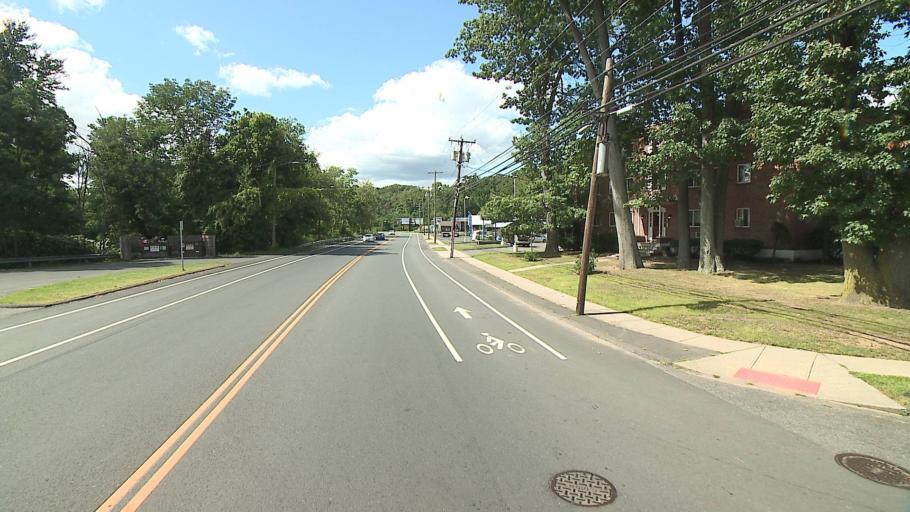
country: US
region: Connecticut
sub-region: Hartford County
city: East Hartford
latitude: 41.7829
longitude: -72.5928
